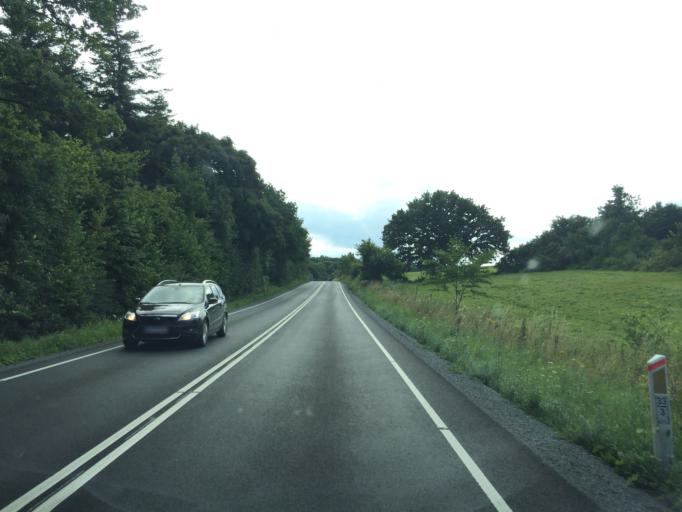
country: DK
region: South Denmark
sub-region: Faaborg-Midtfyn Kommune
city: Faaborg
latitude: 55.1450
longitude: 10.2635
